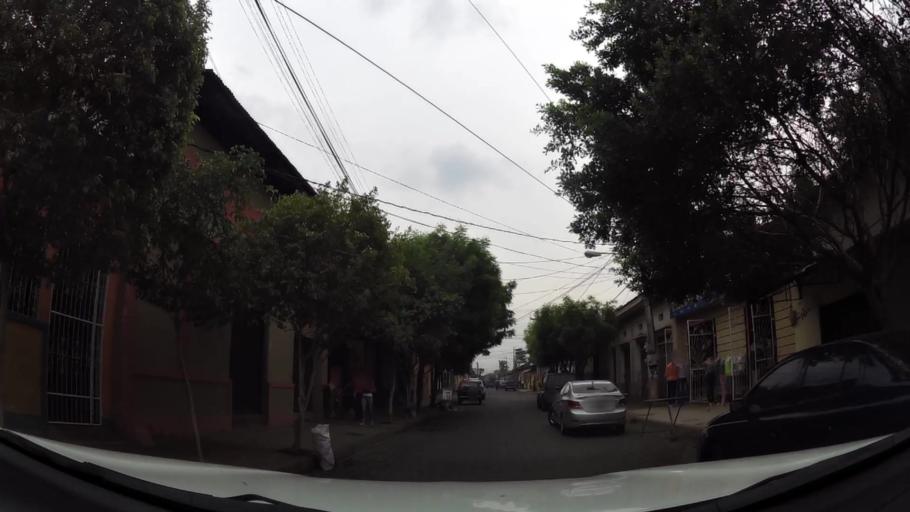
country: NI
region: Leon
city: Leon
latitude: 12.4401
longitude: -86.8722
